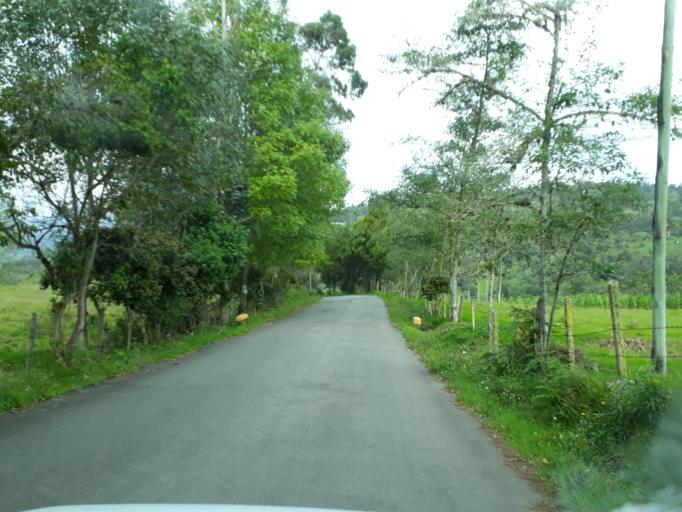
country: CO
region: Cundinamarca
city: Junin
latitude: 4.8073
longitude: -73.6765
